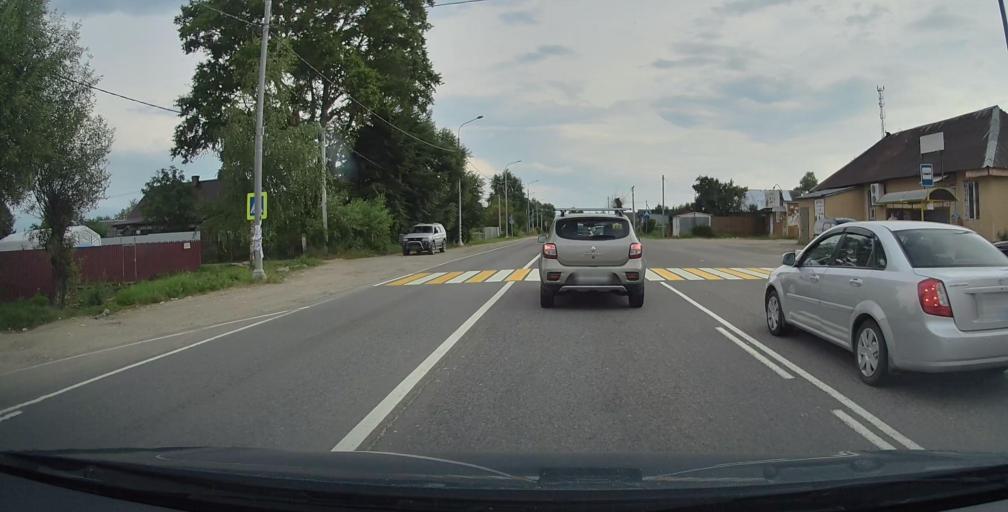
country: RU
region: Moskovskaya
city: Shemetovo
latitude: 56.6761
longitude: 38.1466
